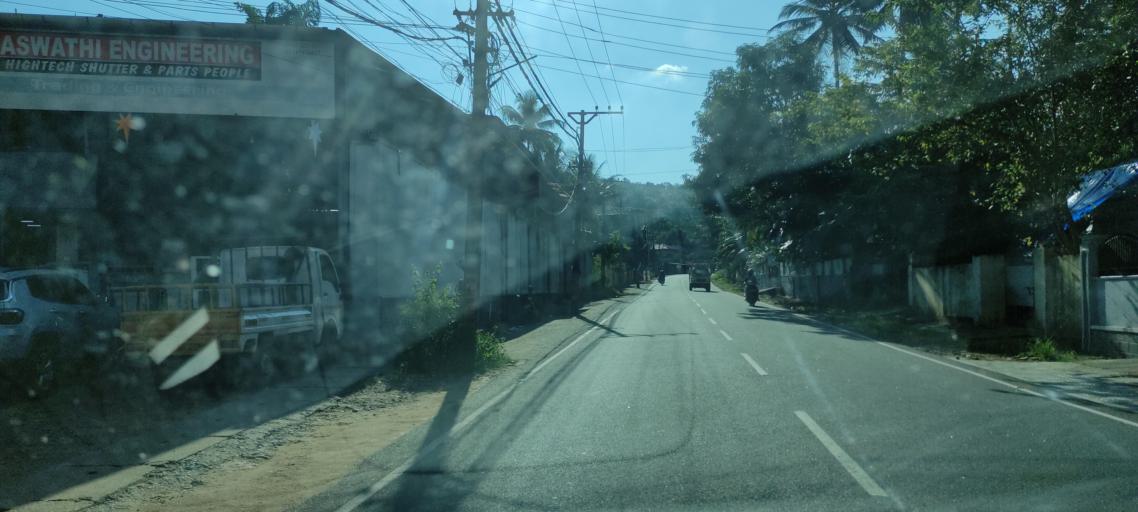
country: IN
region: Kerala
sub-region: Pattanamtitta
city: Pathanamthitta
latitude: 9.2546
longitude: 76.7689
